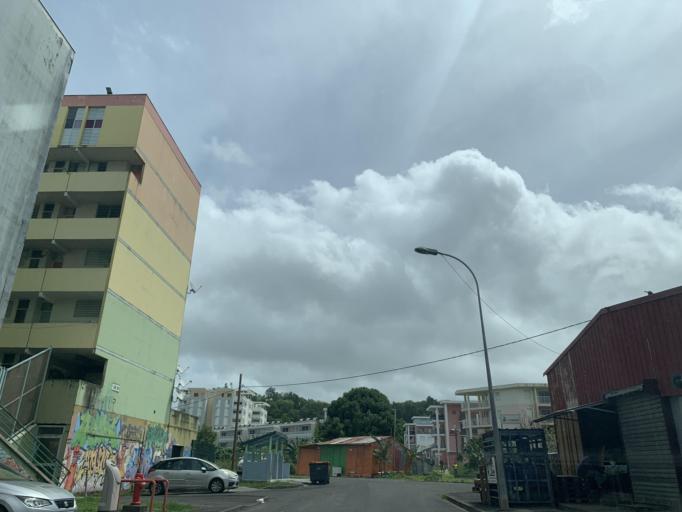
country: GP
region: Guadeloupe
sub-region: Guadeloupe
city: Pointe-a-Pitre
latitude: 16.2406
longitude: -61.5302
